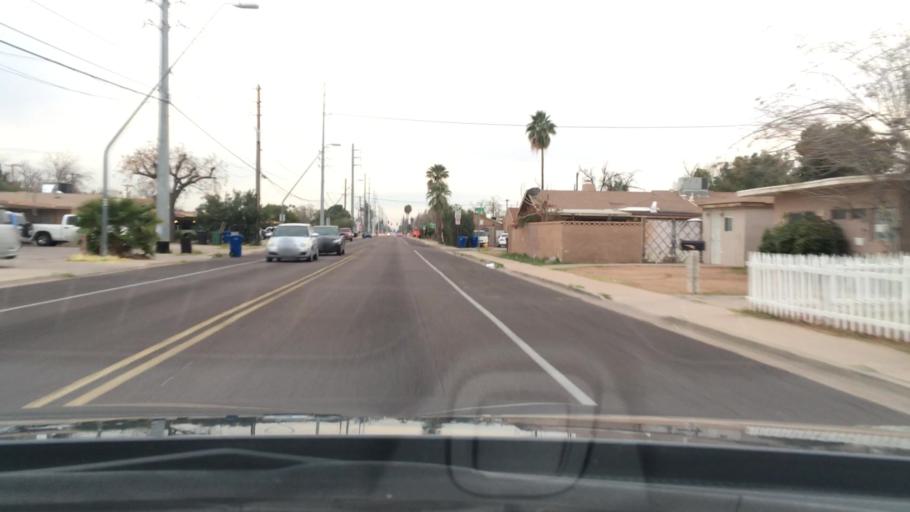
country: US
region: Arizona
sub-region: Maricopa County
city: Mesa
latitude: 33.4189
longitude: -111.8141
